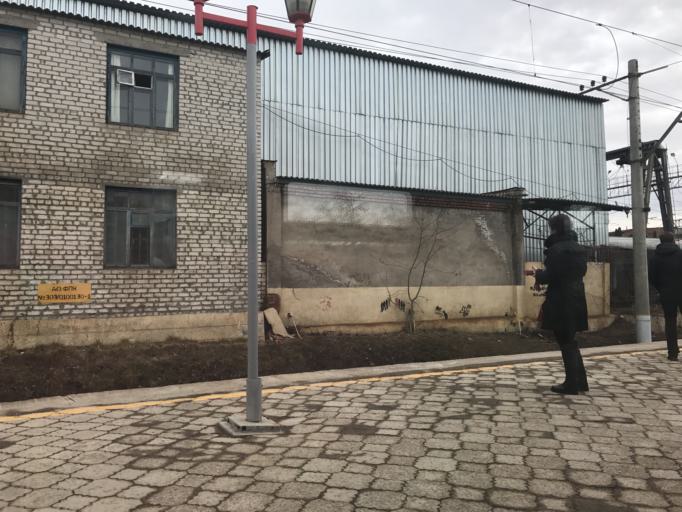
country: RU
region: Stavropol'skiy
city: Kislovodsk
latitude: 43.9225
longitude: 42.7244
